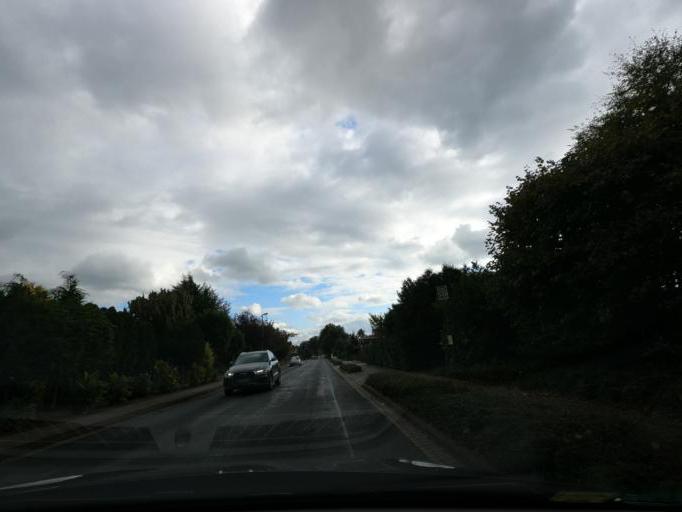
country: DE
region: Lower Saxony
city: Klein Schwulper
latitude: 52.3392
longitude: 10.4332
